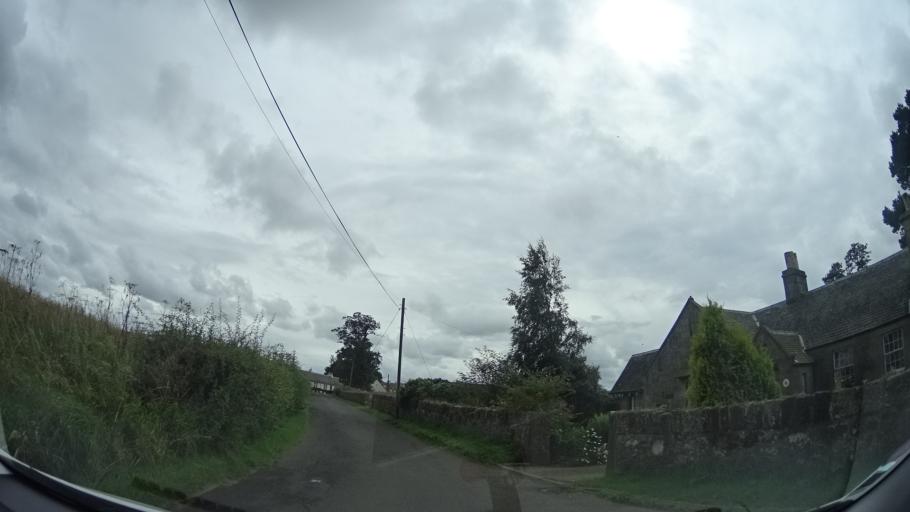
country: GB
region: Scotland
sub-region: Edinburgh
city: Newbridge
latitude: 55.9217
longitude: -3.4203
